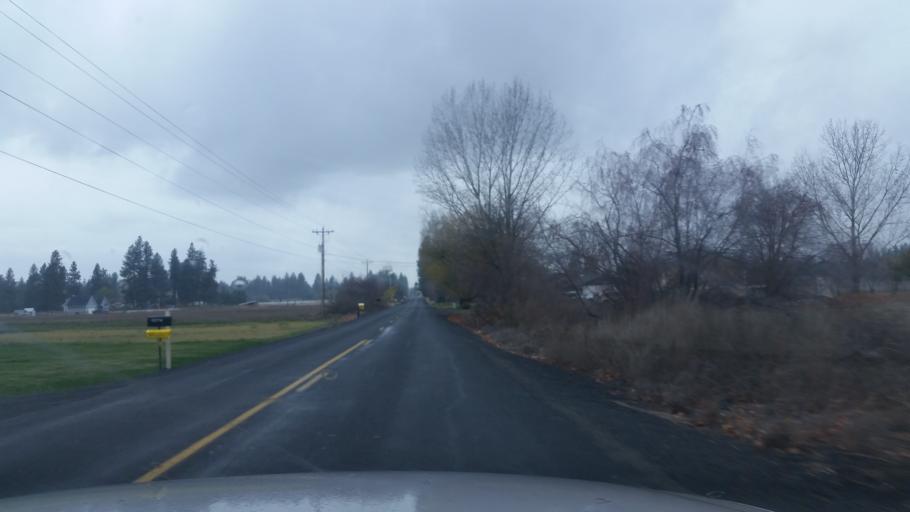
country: US
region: Washington
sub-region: Spokane County
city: Spokane
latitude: 47.5943
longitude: -117.4771
